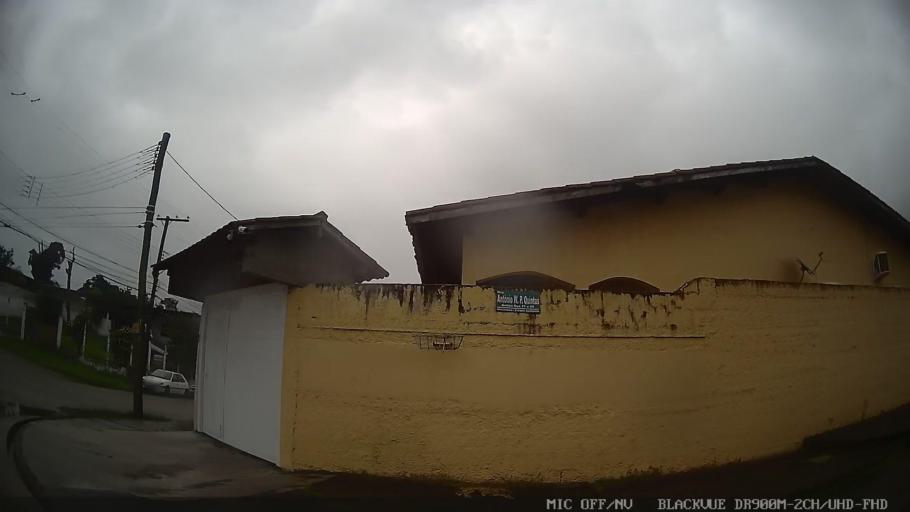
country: BR
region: Sao Paulo
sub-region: Itanhaem
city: Itanhaem
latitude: -24.1802
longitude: -46.8283
